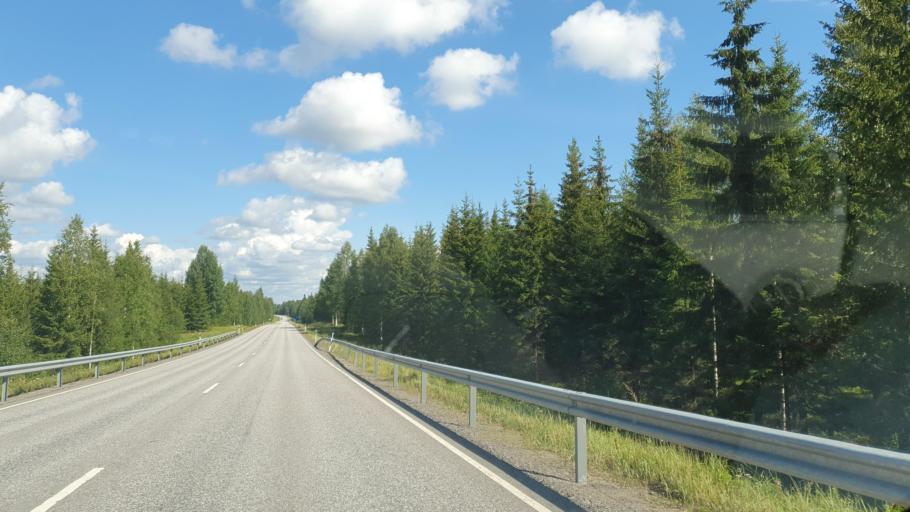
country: FI
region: Northern Savo
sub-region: Ylae-Savo
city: Sonkajaervi
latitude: 63.6883
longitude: 27.3442
